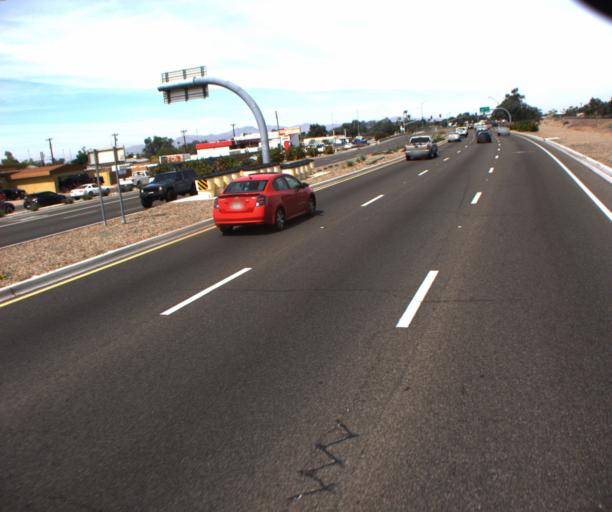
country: US
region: Arizona
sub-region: Maricopa County
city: Sun City
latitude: 33.5932
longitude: -112.2568
